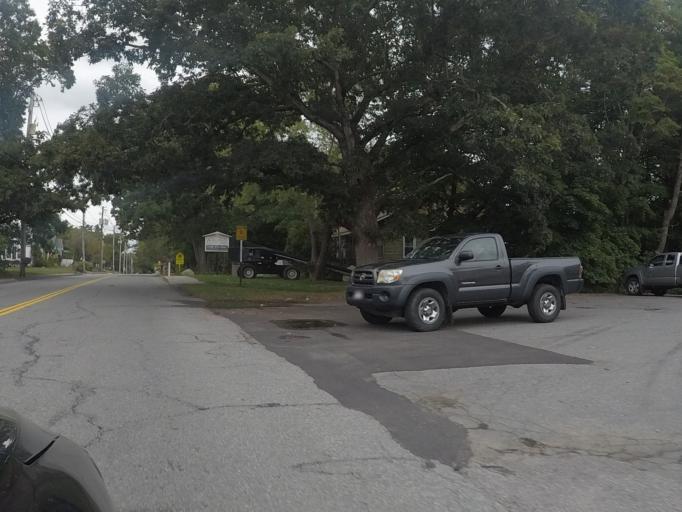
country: US
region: Massachusetts
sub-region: Bristol County
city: Smith Mills
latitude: 41.6432
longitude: -71.0068
